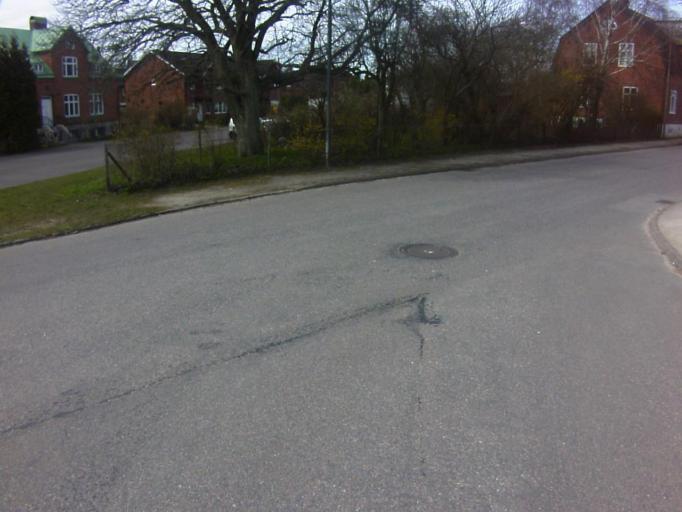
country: SE
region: Skane
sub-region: Kavlinge Kommun
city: Kaevlinge
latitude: 55.7895
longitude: 13.1148
